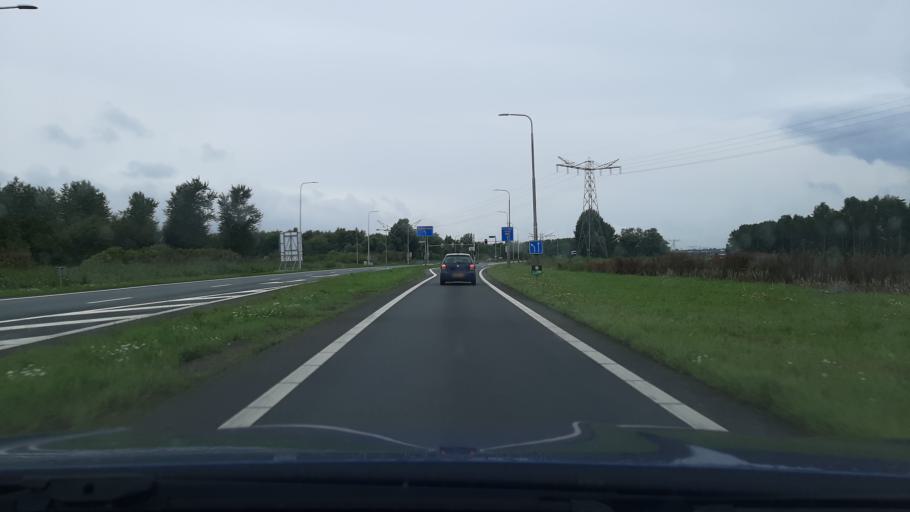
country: NL
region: Utrecht
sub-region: Gemeente Bunschoten
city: Spakenburg
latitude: 52.3089
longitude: 5.3497
